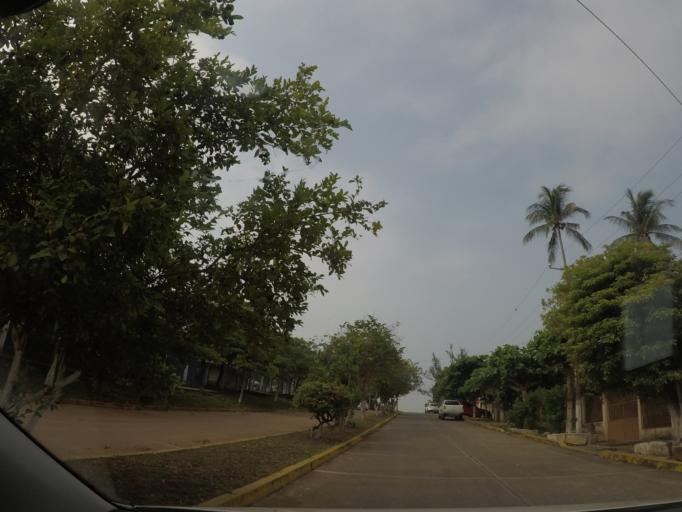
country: MX
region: Oaxaca
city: Matias Romero
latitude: 16.8742
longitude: -95.0478
